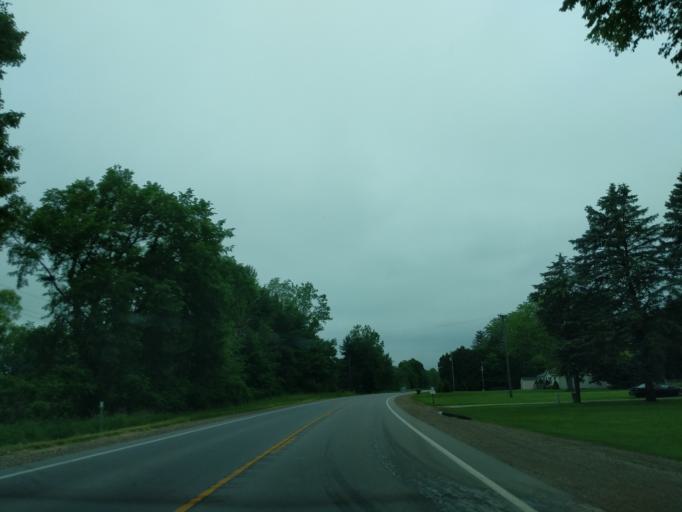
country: US
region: Michigan
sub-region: Branch County
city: Quincy
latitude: 41.9486
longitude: -84.8120
